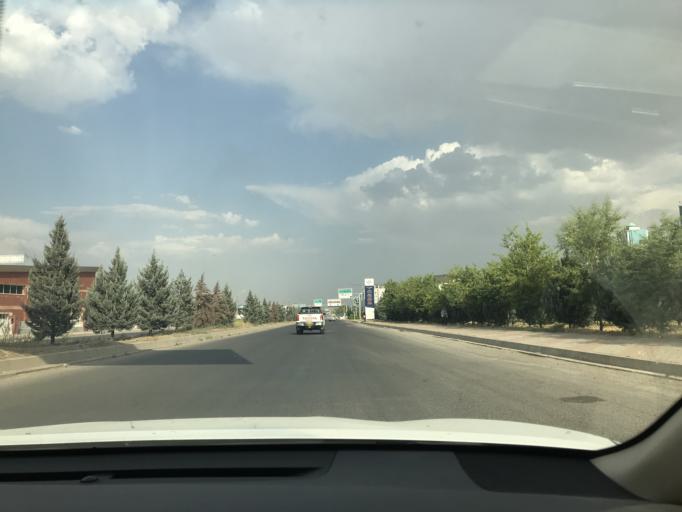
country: IQ
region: Arbil
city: Erbil
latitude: 36.2053
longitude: 43.9644
